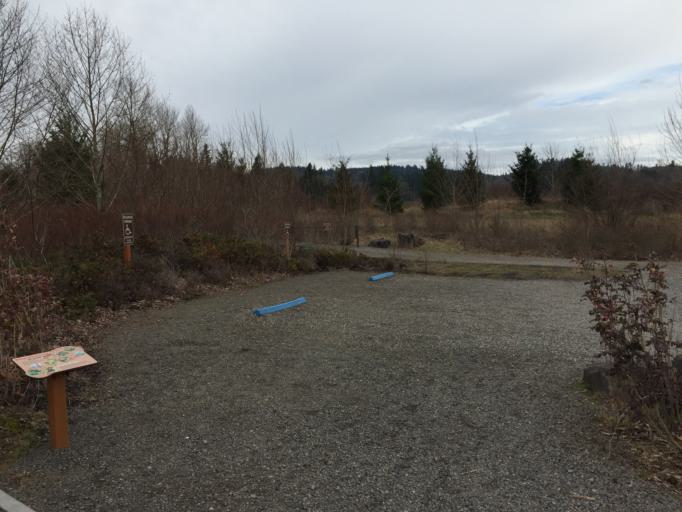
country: US
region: Washington
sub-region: Clark County
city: Washougal
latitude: 45.5703
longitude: -122.3149
